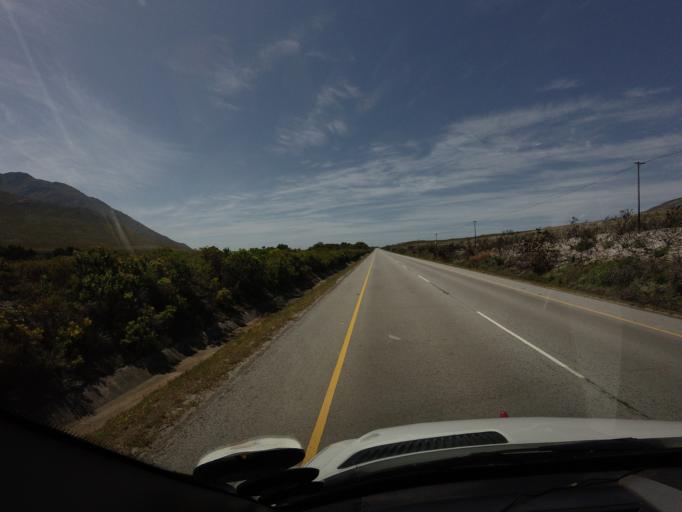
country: ZA
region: Western Cape
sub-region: Overberg District Municipality
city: Grabouw
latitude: -34.3474
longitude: 18.8521
